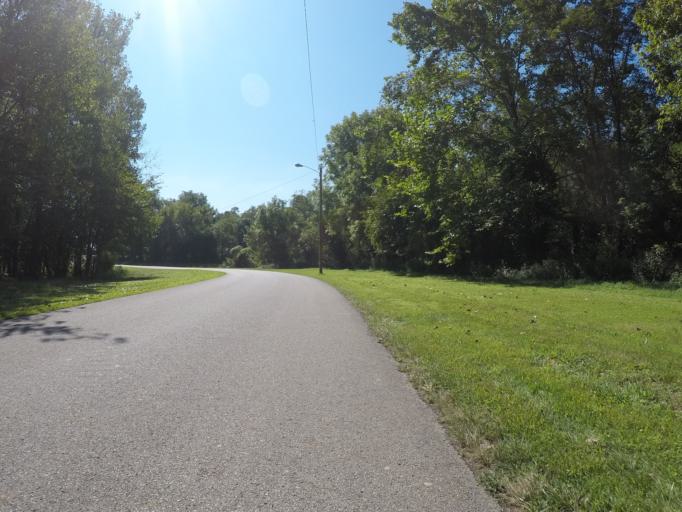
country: US
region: Kentucky
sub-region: Boyd County
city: Catlettsburg
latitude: 38.4105
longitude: -82.5938
